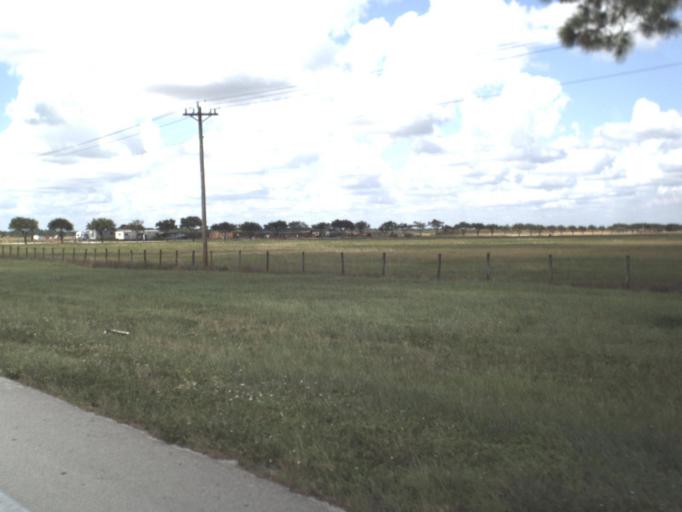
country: US
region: Florida
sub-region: Lee County
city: Lehigh Acres
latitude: 26.5146
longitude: -81.5486
